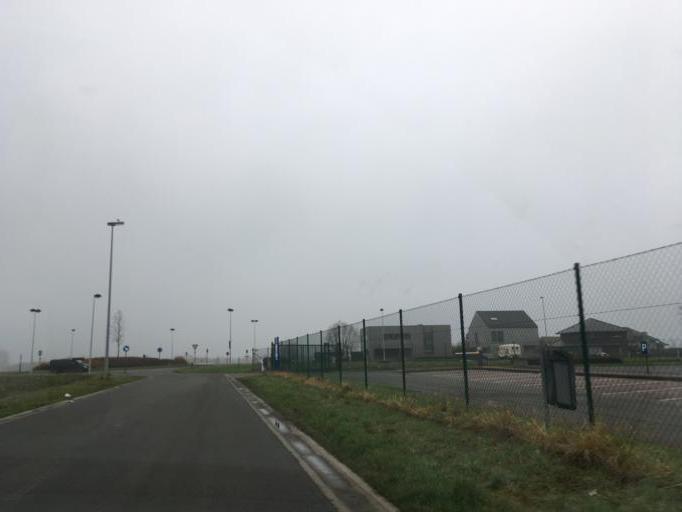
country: BE
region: Flanders
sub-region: Provincie West-Vlaanderen
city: Roeselare
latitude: 50.9711
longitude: 3.1533
